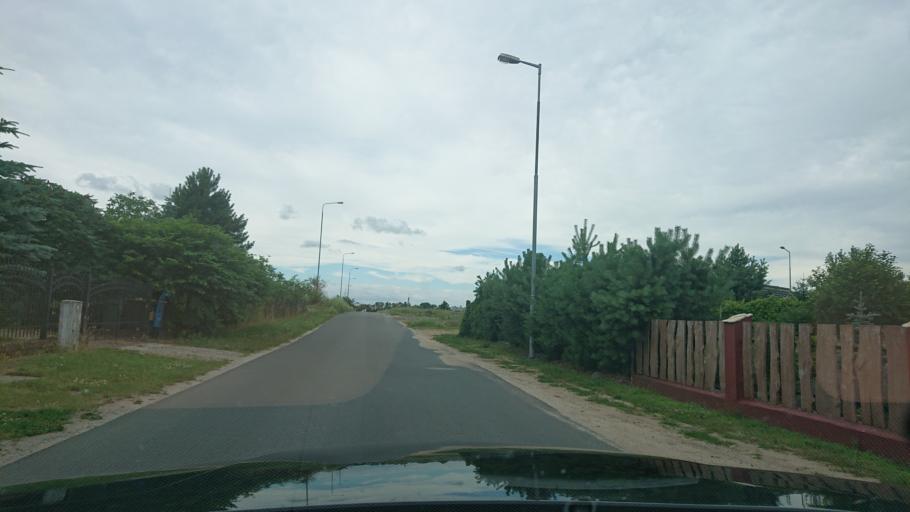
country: PL
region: Greater Poland Voivodeship
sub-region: Powiat gnieznienski
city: Gniezno
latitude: 52.5087
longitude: 17.6084
